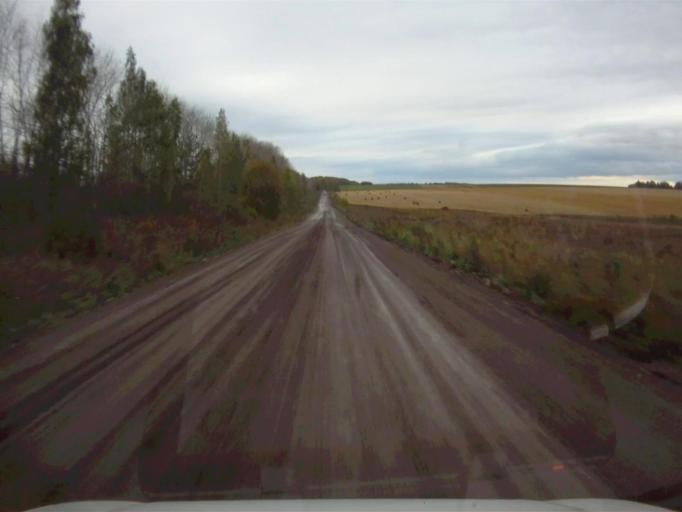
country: RU
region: Sverdlovsk
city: Mikhaylovsk
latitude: 56.1623
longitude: 59.2439
